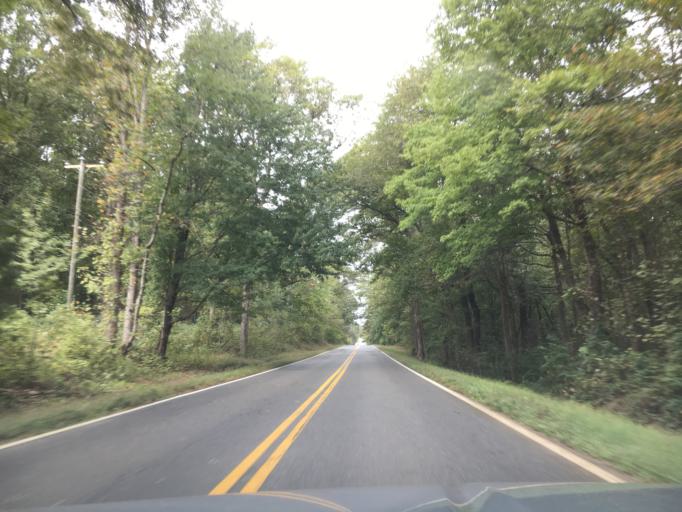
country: US
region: Virginia
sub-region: Goochland County
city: Goochland
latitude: 37.7618
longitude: -77.8764
